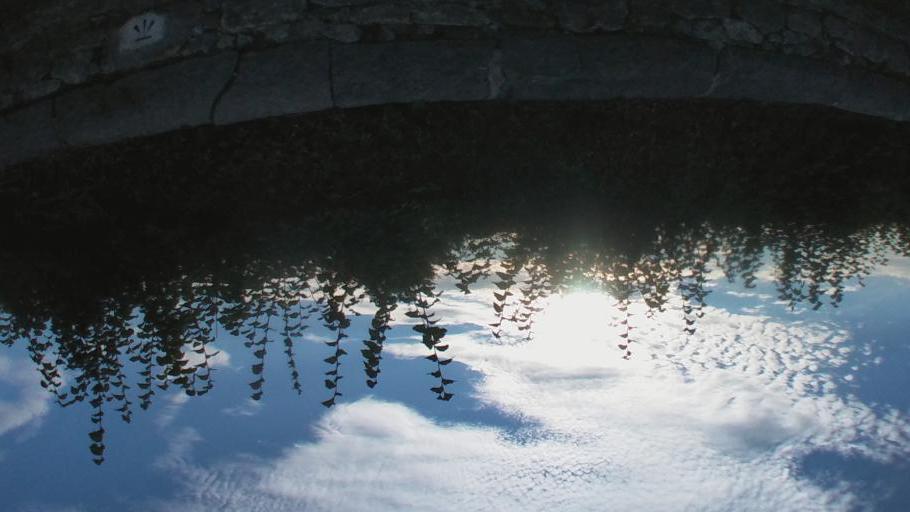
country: IE
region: Leinster
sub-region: Kilkenny
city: Kilkenny
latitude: 52.6876
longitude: -7.2188
